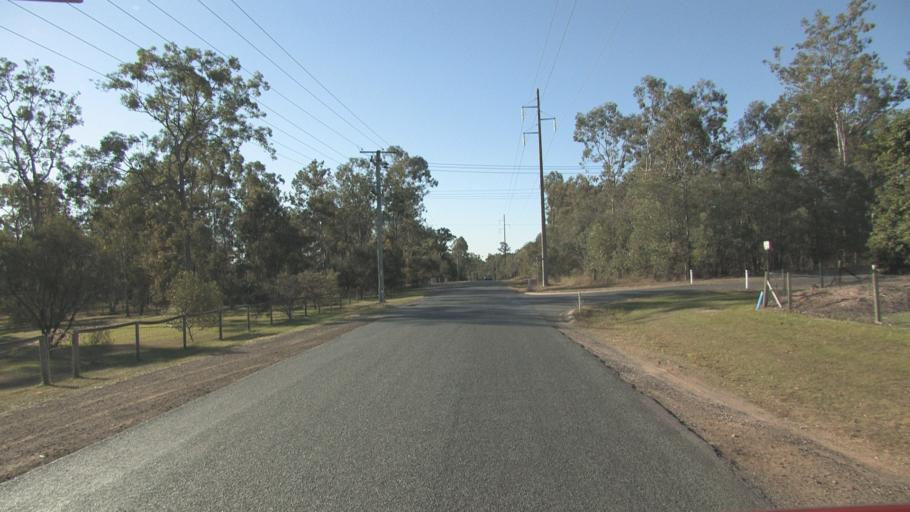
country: AU
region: Queensland
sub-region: Logan
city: North Maclean
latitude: -27.7982
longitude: 153.0417
